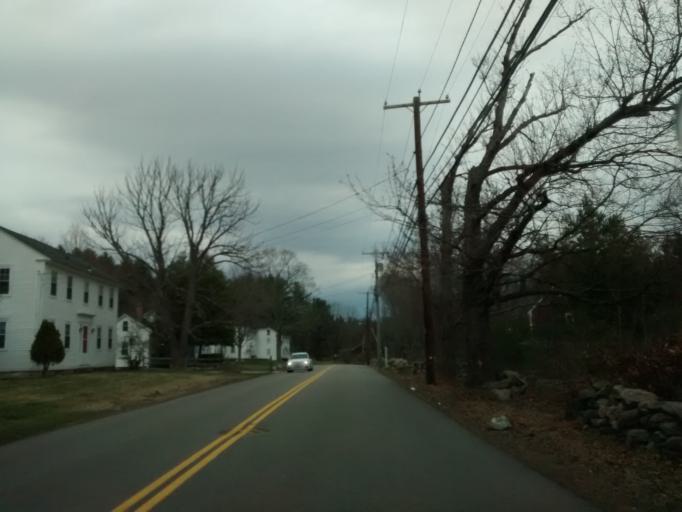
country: US
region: Massachusetts
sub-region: Worcester County
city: Grafton
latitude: 42.1958
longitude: -71.6975
